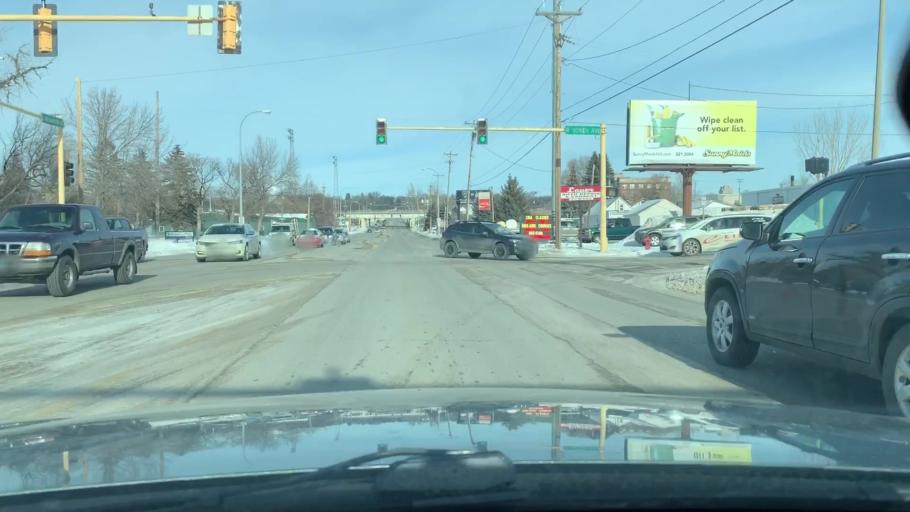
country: US
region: North Dakota
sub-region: Burleigh County
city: Bismarck
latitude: 46.8020
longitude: -100.7944
